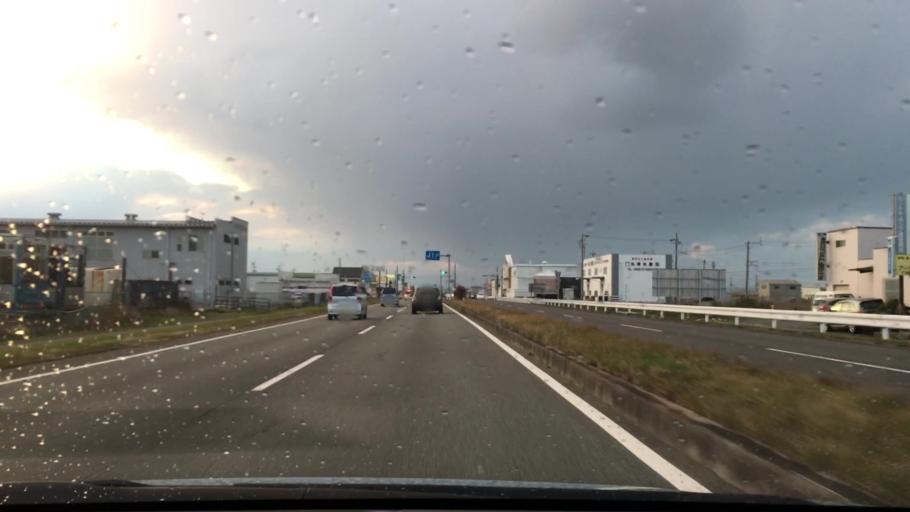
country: JP
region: Mie
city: Ise
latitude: 34.5375
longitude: 136.6732
